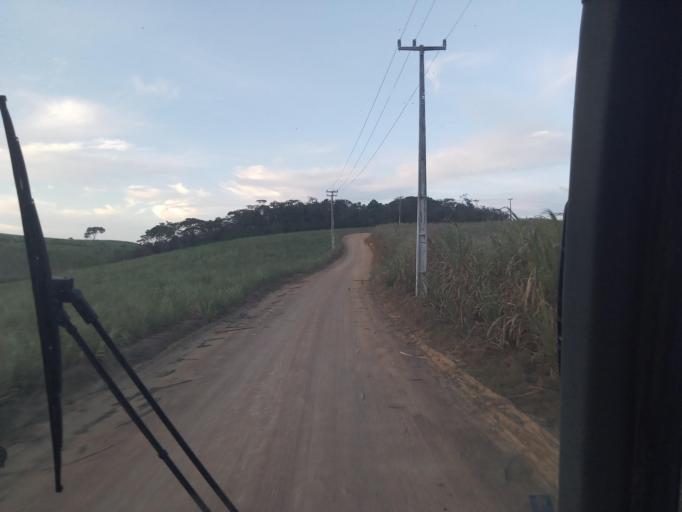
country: BR
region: Pernambuco
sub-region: Vitoria De Santo Antao
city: Vitoria de Santo Antao
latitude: -8.1601
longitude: -35.2581
